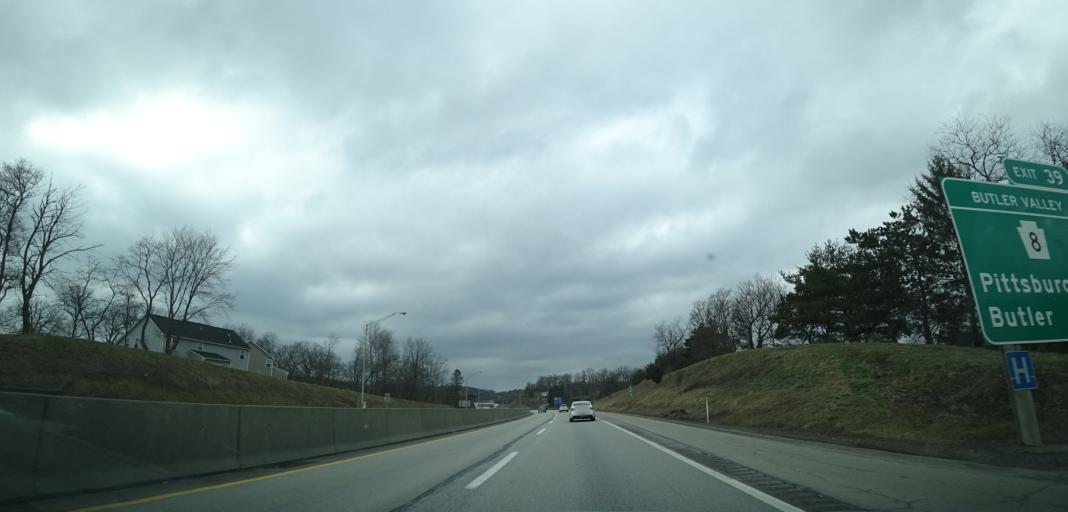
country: US
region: Pennsylvania
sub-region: Allegheny County
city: Gibsonia
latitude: 40.6060
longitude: -79.9400
